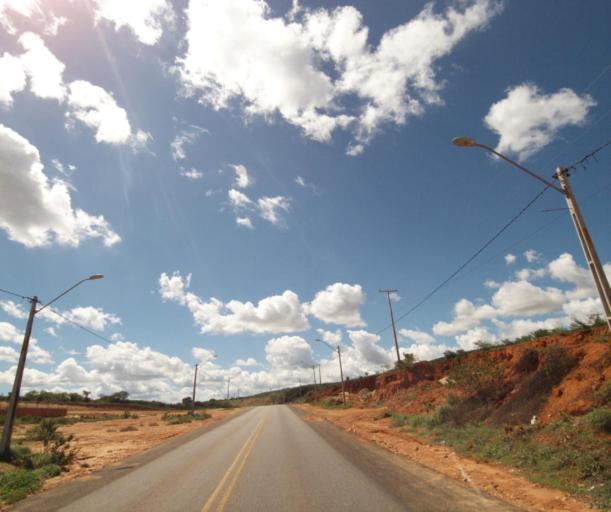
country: BR
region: Bahia
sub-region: Cacule
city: Cacule
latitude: -14.2035
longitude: -42.1244
